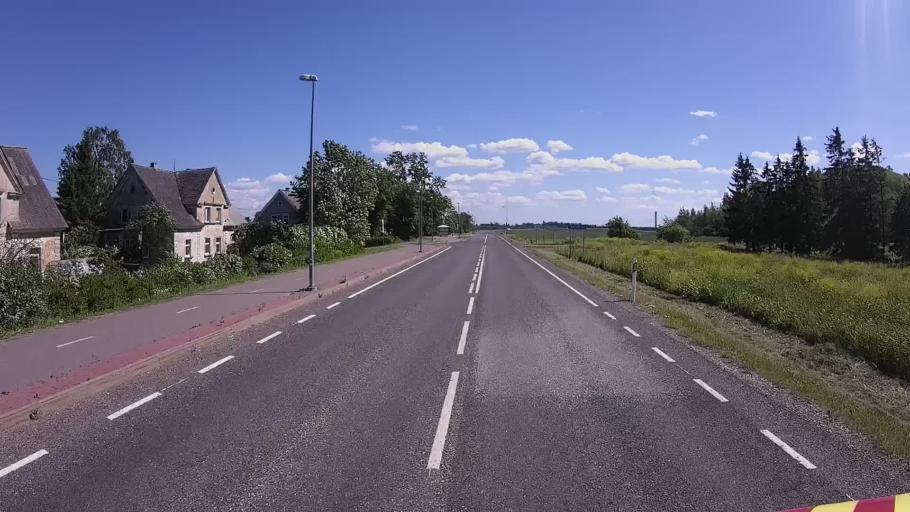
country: EE
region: Ida-Virumaa
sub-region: Kohtla-Jaerve linn
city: Kohtla-Jarve
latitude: 59.3970
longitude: 27.3417
